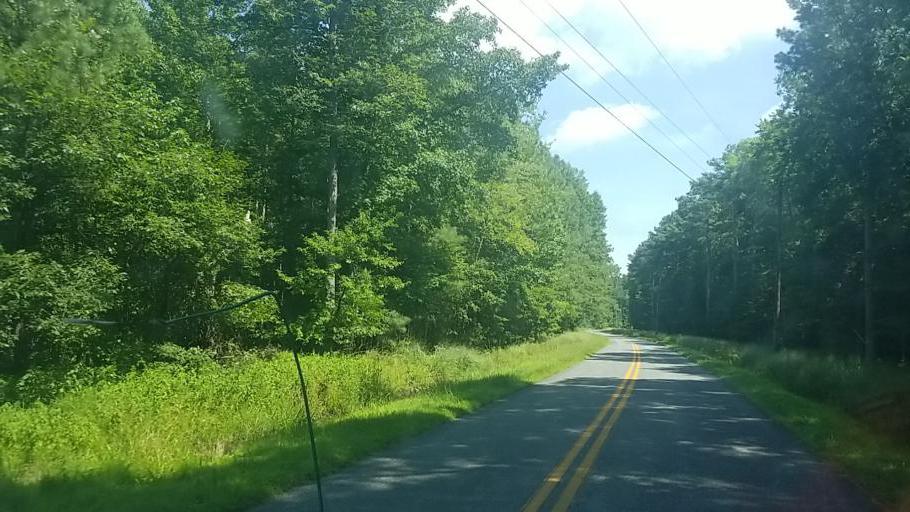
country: US
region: Maryland
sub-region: Wicomico County
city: Hebron
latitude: 38.4272
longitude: -75.8801
